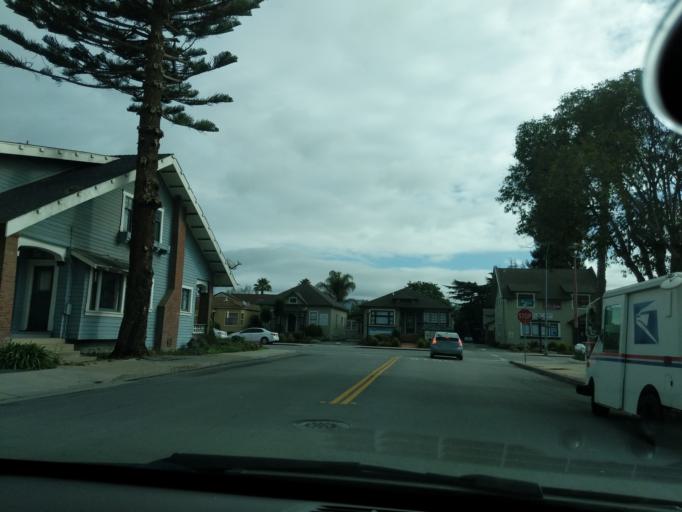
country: US
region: California
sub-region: Santa Cruz County
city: Watsonville
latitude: 36.9138
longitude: -121.7586
